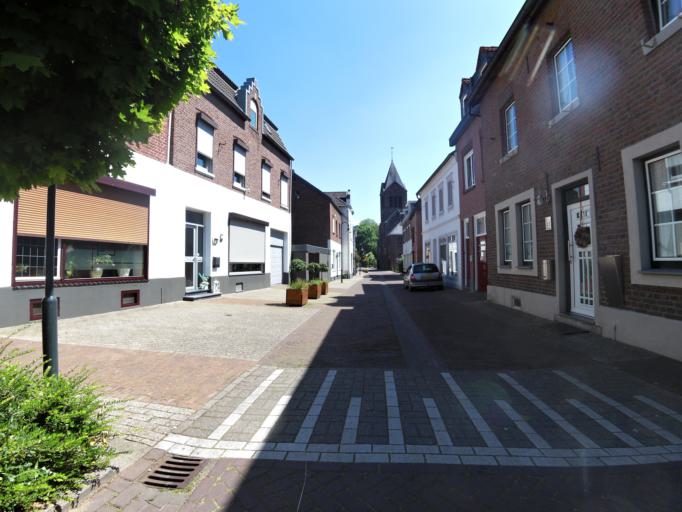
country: DE
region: North Rhine-Westphalia
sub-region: Regierungsbezirk Koln
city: Ubach-Palenberg
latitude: 50.9166
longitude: 6.0871
